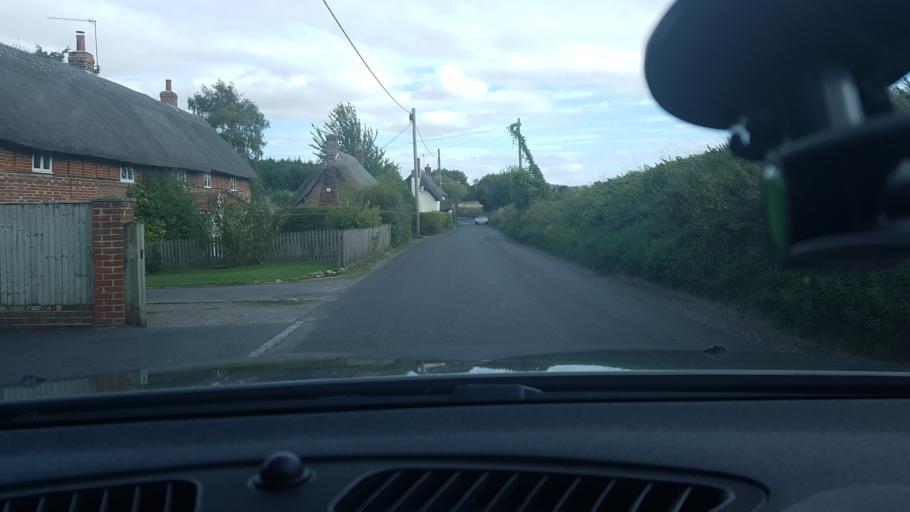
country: GB
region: England
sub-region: Wiltshire
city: Great Bedwyn
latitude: 51.3771
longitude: -1.5954
